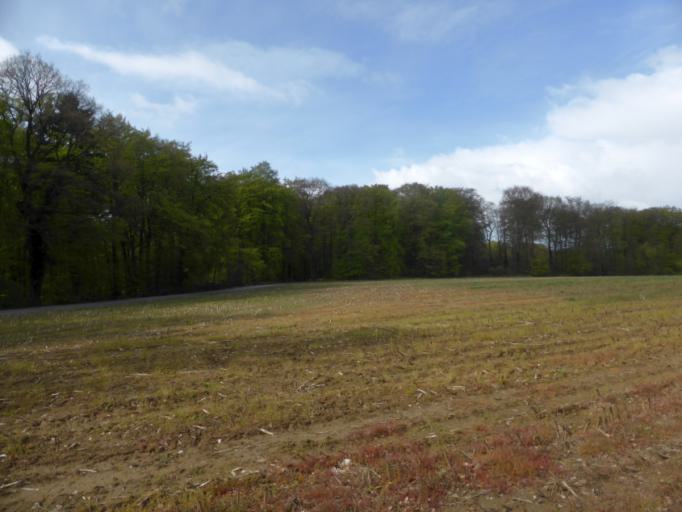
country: LU
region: Luxembourg
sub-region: Canton de Luxembourg
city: Steinsel
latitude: 49.6739
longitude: 6.1056
